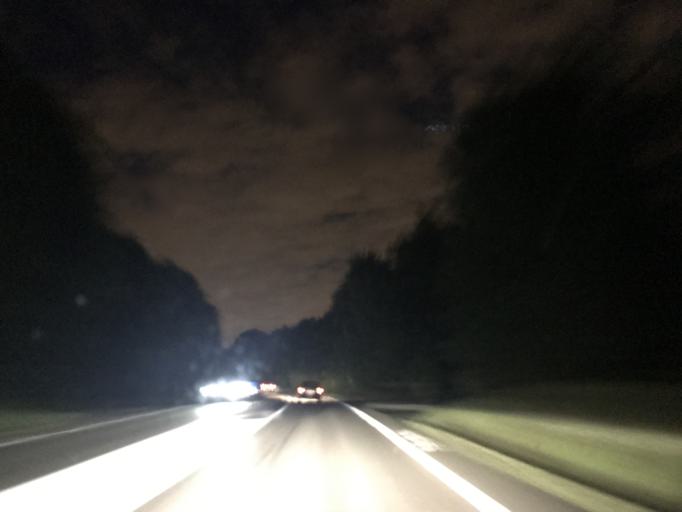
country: FR
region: Ile-de-France
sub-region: Departement des Yvelines
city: Le Mesnil-le-Roi
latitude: 48.9416
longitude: 2.1158
